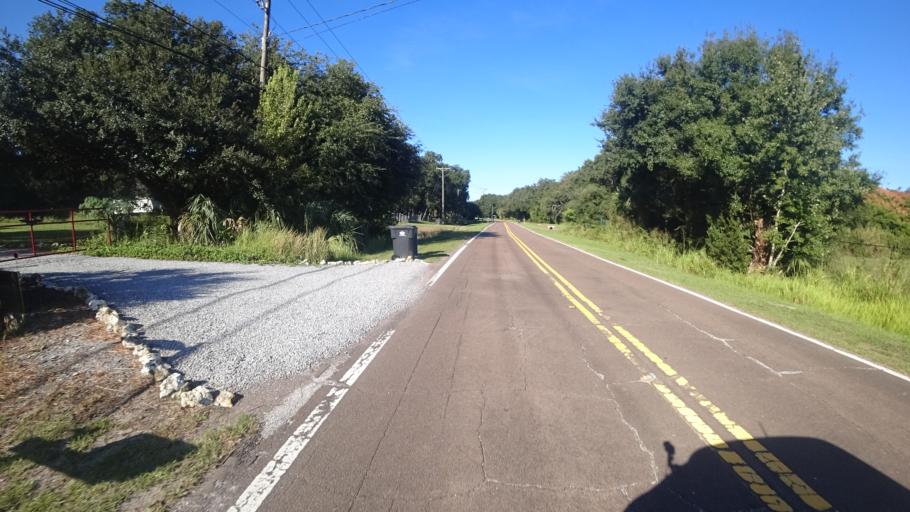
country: US
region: Florida
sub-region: Hillsborough County
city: Ruskin
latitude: 27.6478
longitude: -82.4136
